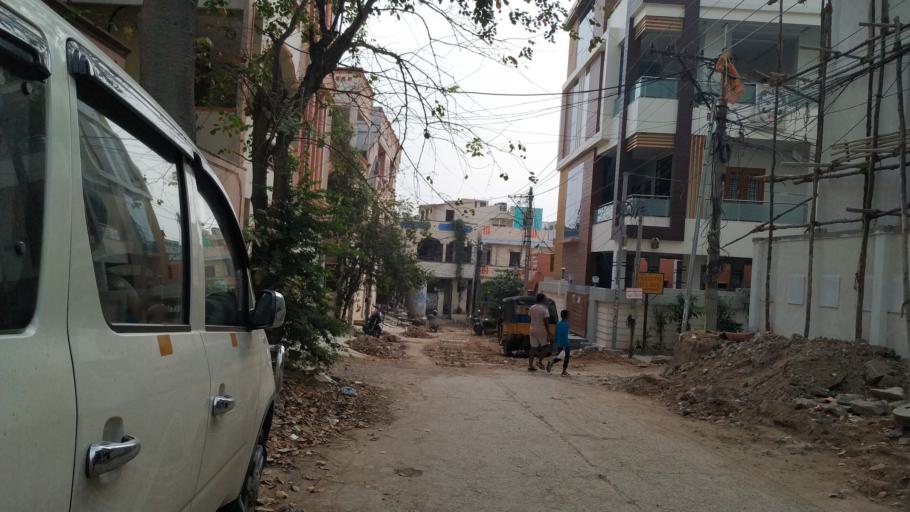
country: IN
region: Telangana
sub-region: Medak
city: Serilingampalle
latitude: 17.4929
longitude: 78.3206
